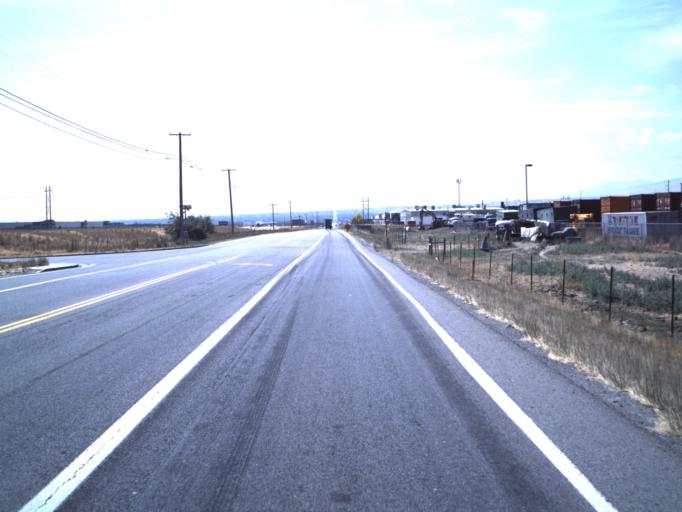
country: US
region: Utah
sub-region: Salt Lake County
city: West Valley City
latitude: 40.7479
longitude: -112.0250
